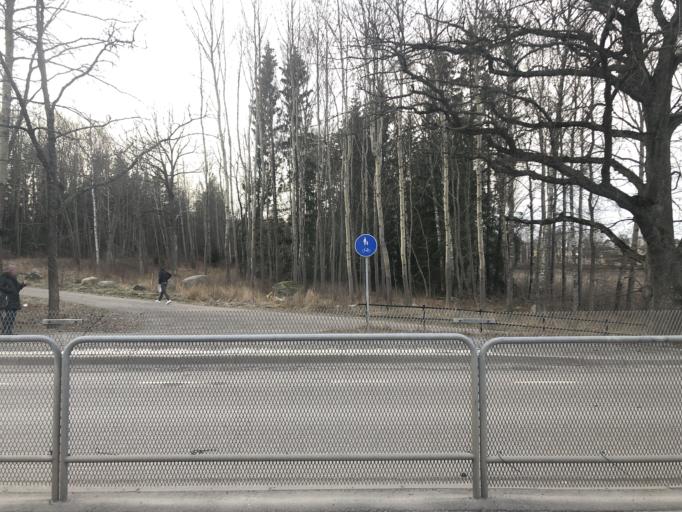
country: SE
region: Stockholm
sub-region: Jarfalla Kommun
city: Jakobsberg
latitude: 59.4127
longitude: 17.7968
